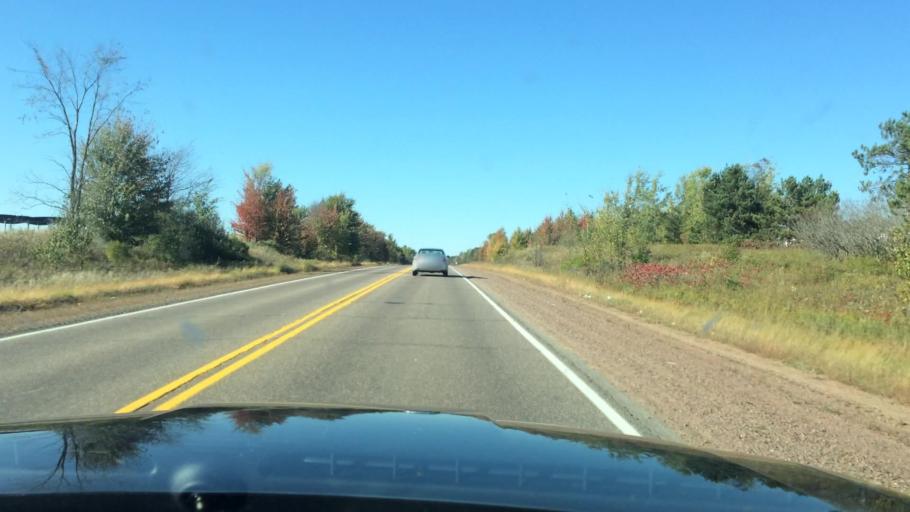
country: US
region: Wisconsin
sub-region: Marathon County
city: Wausau
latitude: 45.0064
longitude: -89.6724
